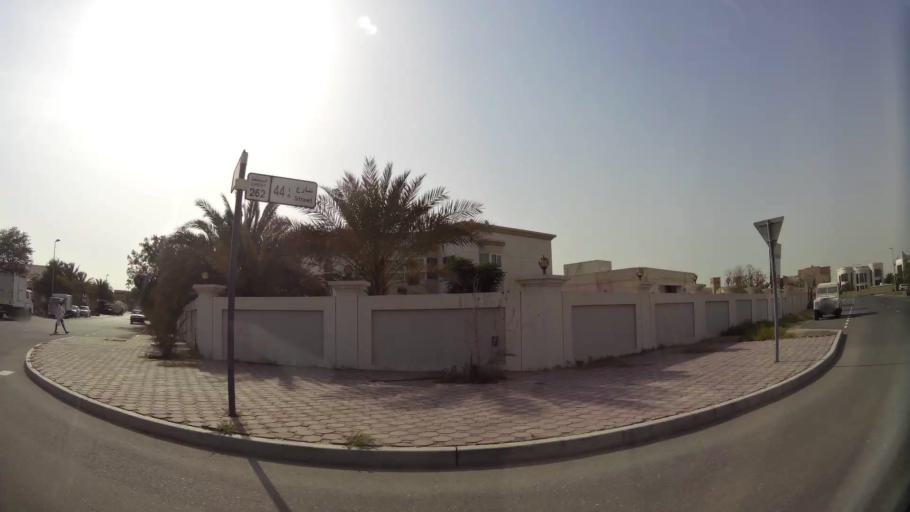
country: AE
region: Ash Shariqah
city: Sharjah
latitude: 25.2525
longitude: 55.4530
